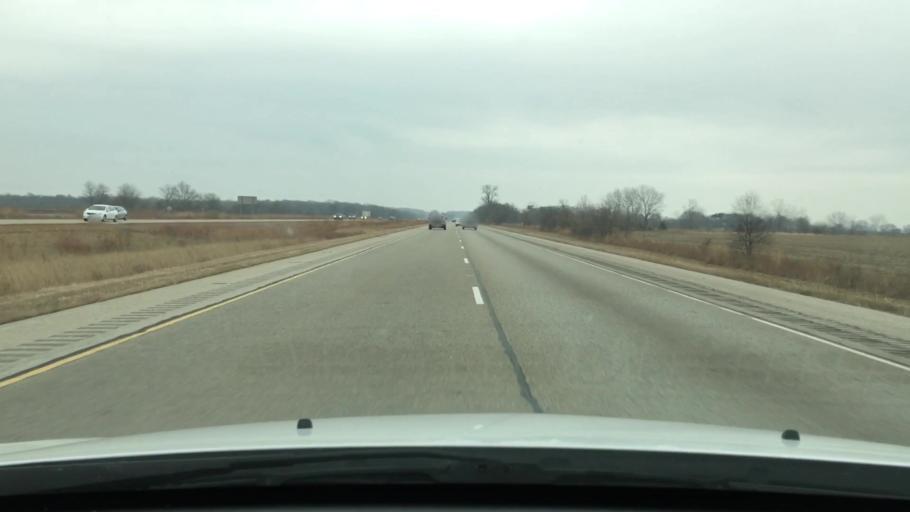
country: US
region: Illinois
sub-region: Logan County
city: Atlanta
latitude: 40.3325
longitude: -89.1474
